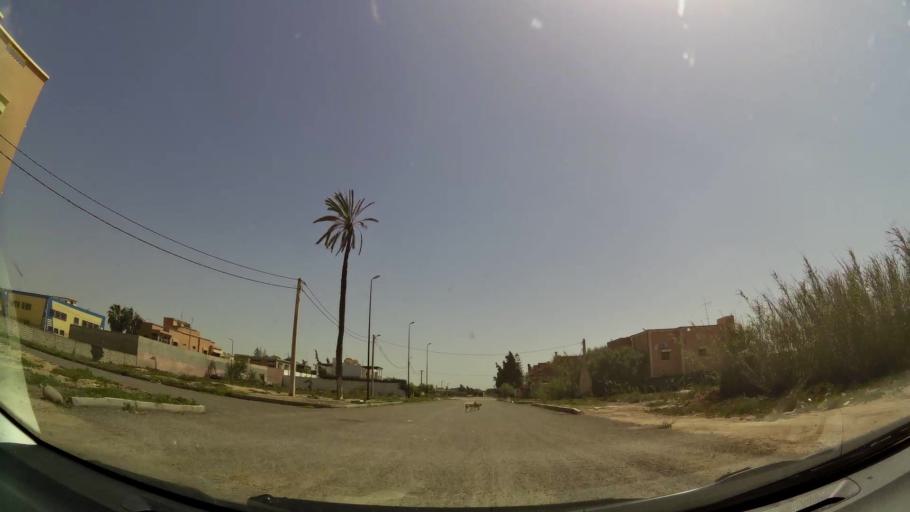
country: MA
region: Souss-Massa-Draa
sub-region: Inezgane-Ait Mellou
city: Inezgane
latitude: 30.3470
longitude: -9.5143
